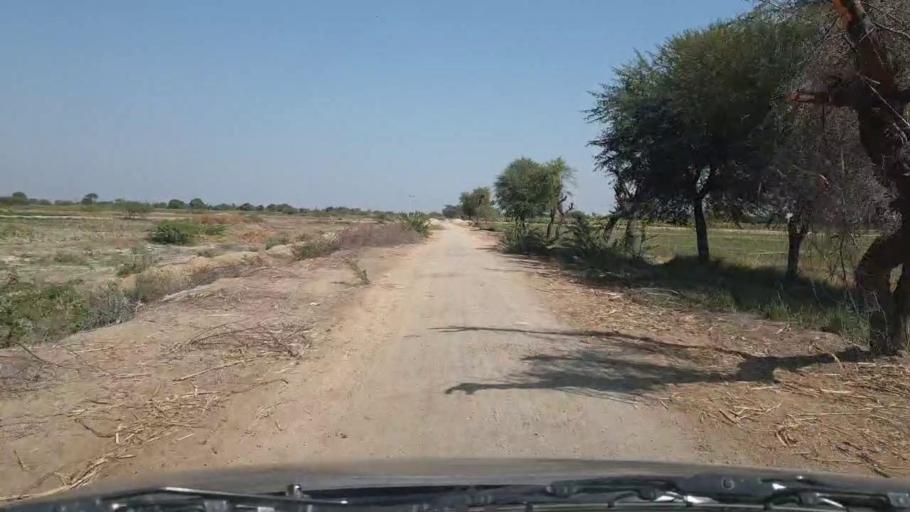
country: PK
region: Sindh
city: Digri
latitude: 25.2303
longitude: 69.2444
